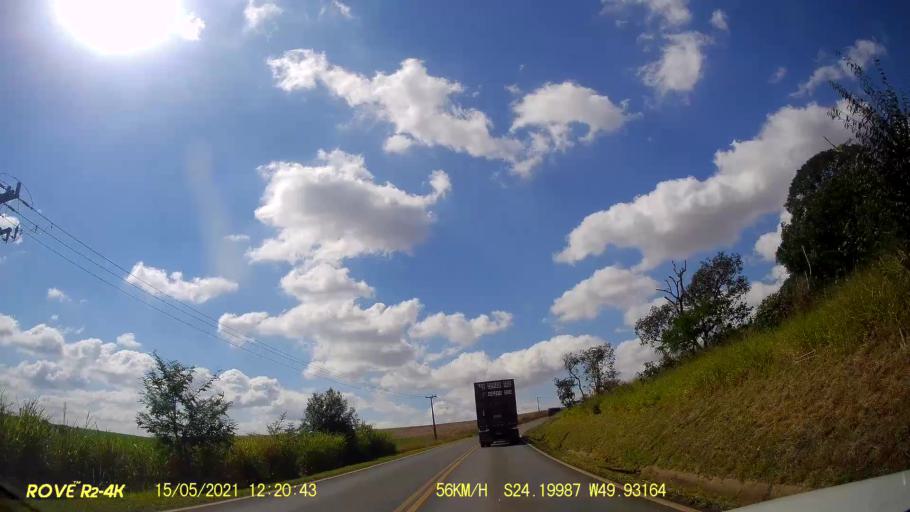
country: BR
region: Parana
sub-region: Jaguariaiva
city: Jaguariaiva
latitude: -24.1995
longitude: -49.9310
